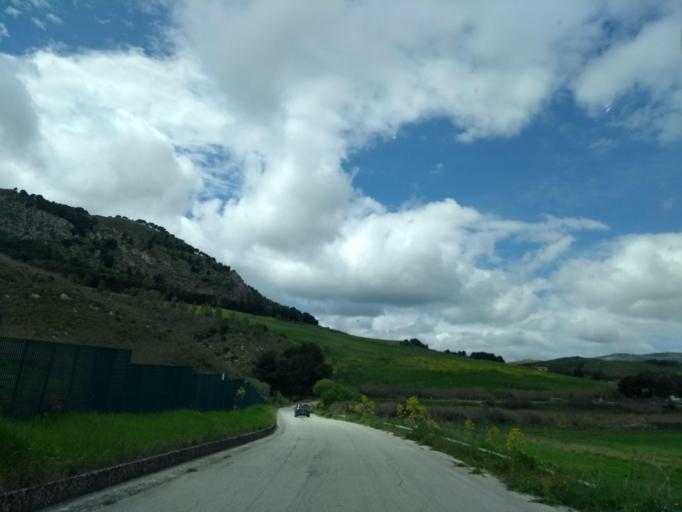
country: IT
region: Sicily
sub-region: Trapani
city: Calatafimi
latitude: 37.9442
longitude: 12.8353
